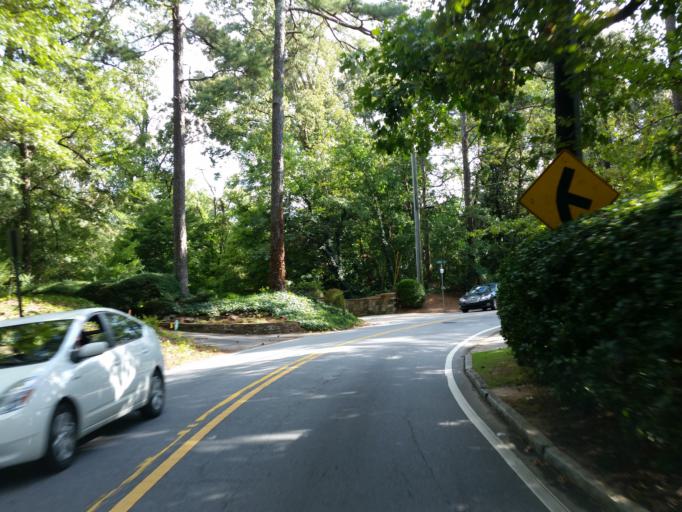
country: US
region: Georgia
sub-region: Cobb County
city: Vinings
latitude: 33.8754
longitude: -84.4140
